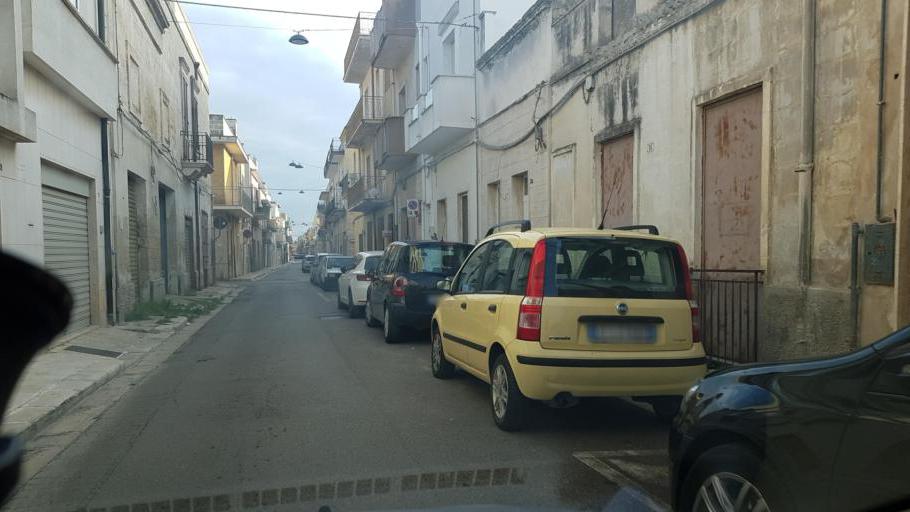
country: IT
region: Apulia
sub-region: Provincia di Brindisi
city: Francavilla Fontana
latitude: 40.5304
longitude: 17.5788
